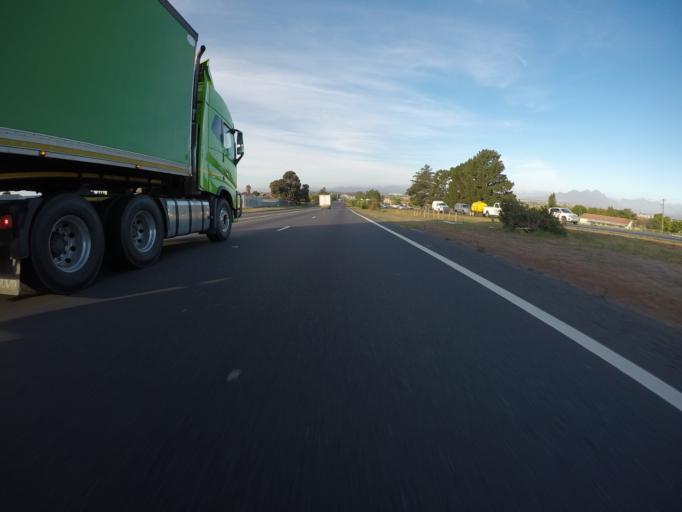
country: ZA
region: Western Cape
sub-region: City of Cape Town
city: Kraaifontein
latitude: -33.8557
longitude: 18.6989
